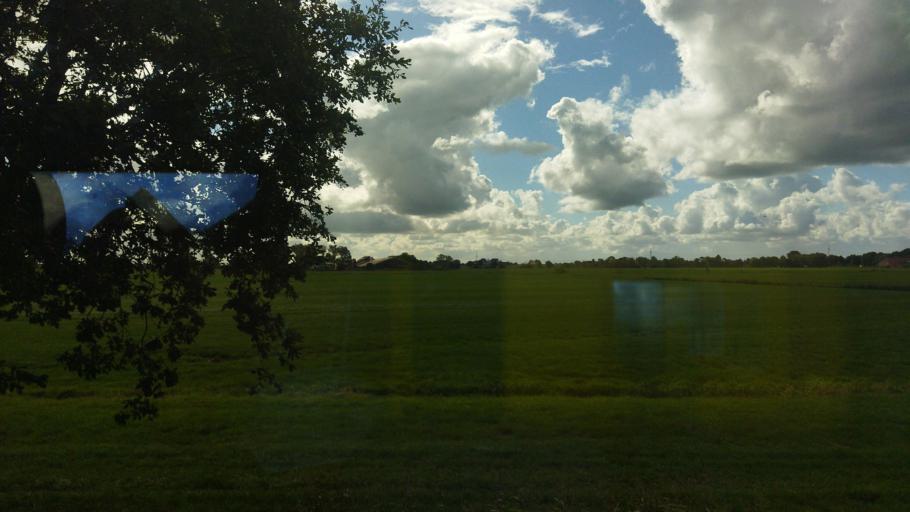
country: DE
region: Lower Saxony
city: Jemgum
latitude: 53.3284
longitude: 7.3660
